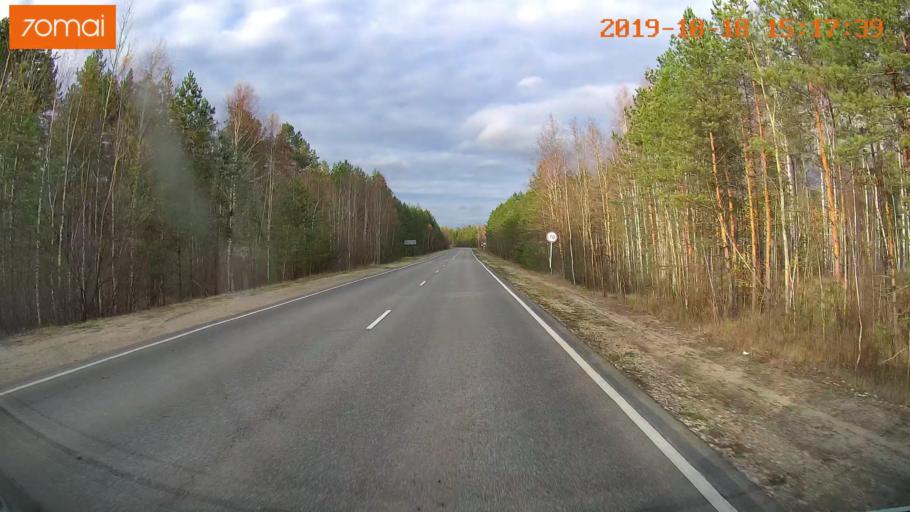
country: RU
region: Vladimir
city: Anopino
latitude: 55.6530
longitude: 40.7270
